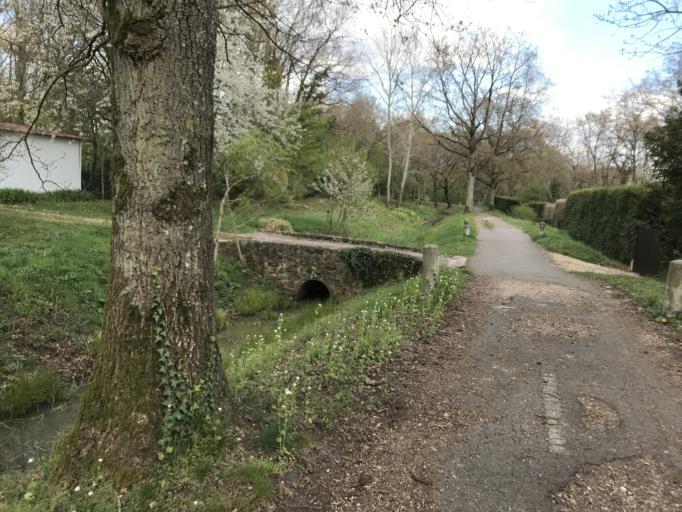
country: FR
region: Ile-de-France
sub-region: Departement de l'Essonne
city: Vauhallan
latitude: 48.7363
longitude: 2.2005
